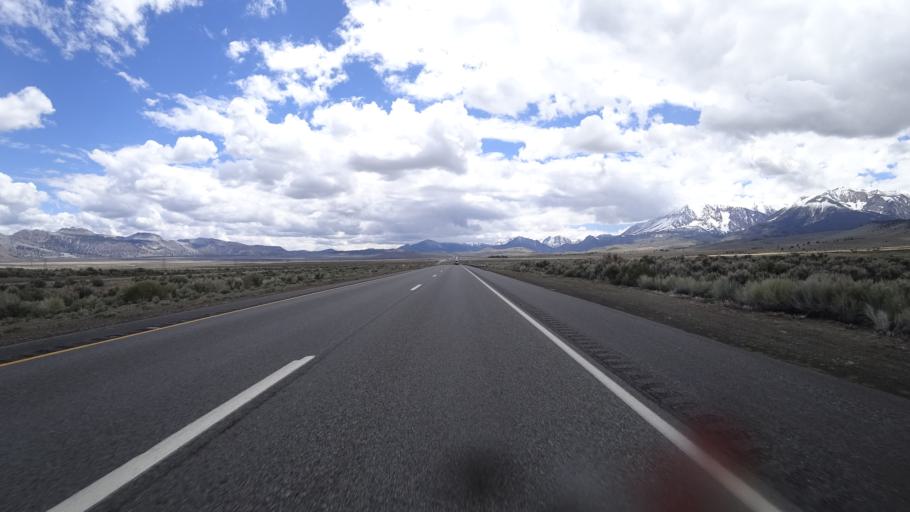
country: US
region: California
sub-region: Mono County
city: Mammoth Lakes
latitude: 37.9161
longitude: -119.0970
